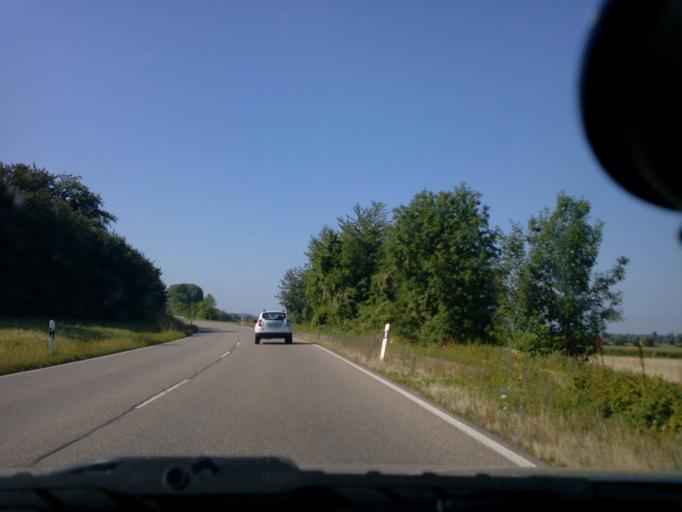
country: DE
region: Baden-Wuerttemberg
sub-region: Karlsruhe Region
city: Weingarten
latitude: 49.0685
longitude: 8.5398
